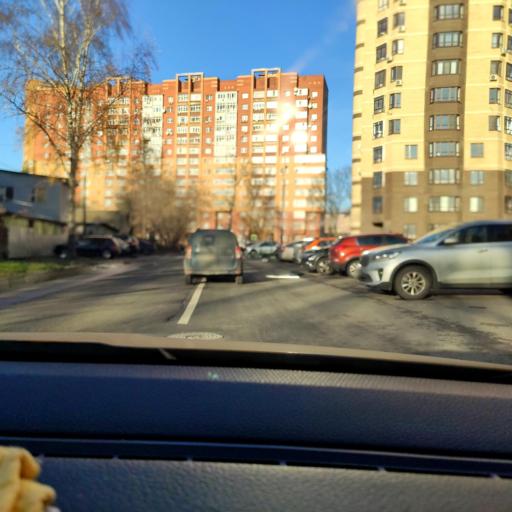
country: RU
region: Moscow
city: Yaroslavskiy
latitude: 55.8943
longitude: 37.7098
